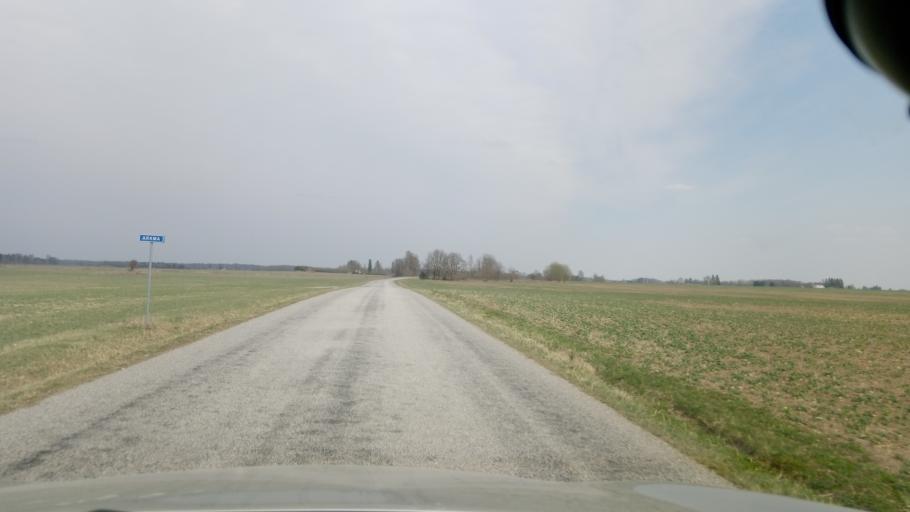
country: EE
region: Viljandimaa
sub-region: Vohma linn
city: Vohma
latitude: 58.6742
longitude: 25.5716
